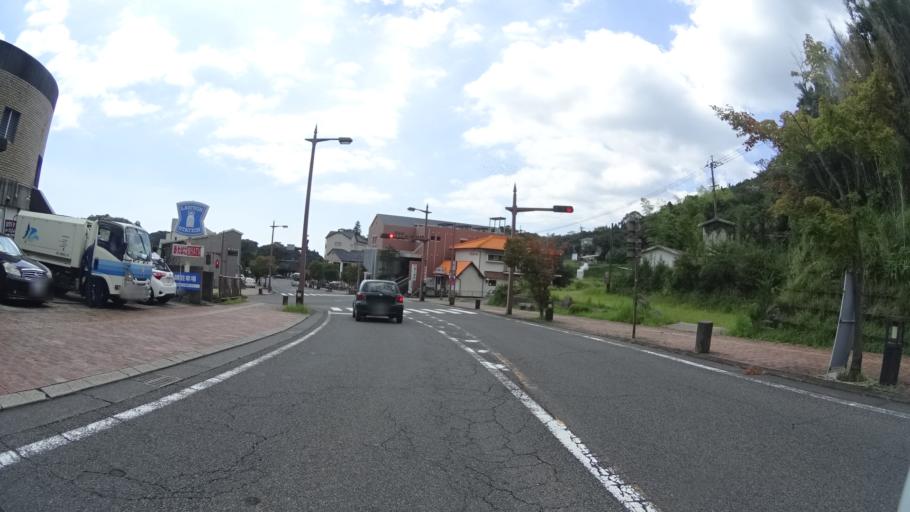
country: JP
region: Kagoshima
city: Kokubu-matsuki
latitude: 31.8933
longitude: 130.8273
